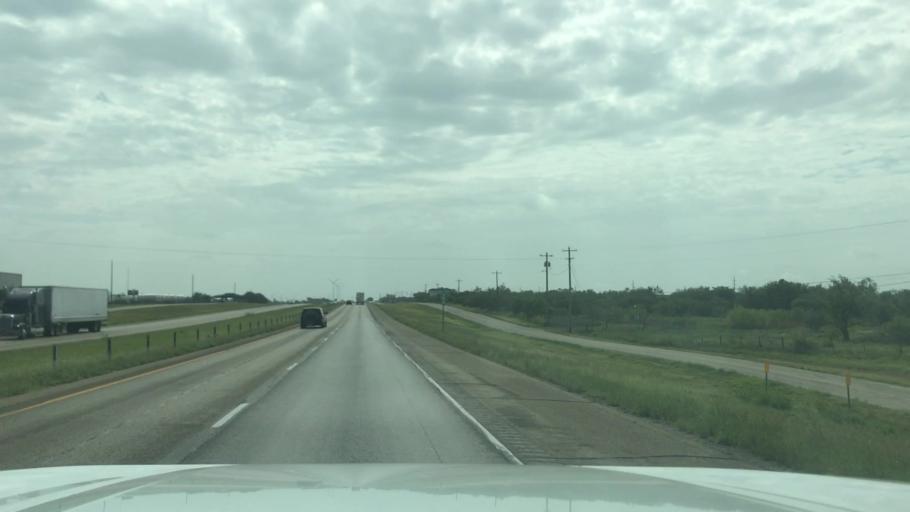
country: US
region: Texas
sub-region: Callahan County
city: Clyde
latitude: 32.4197
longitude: -99.5361
